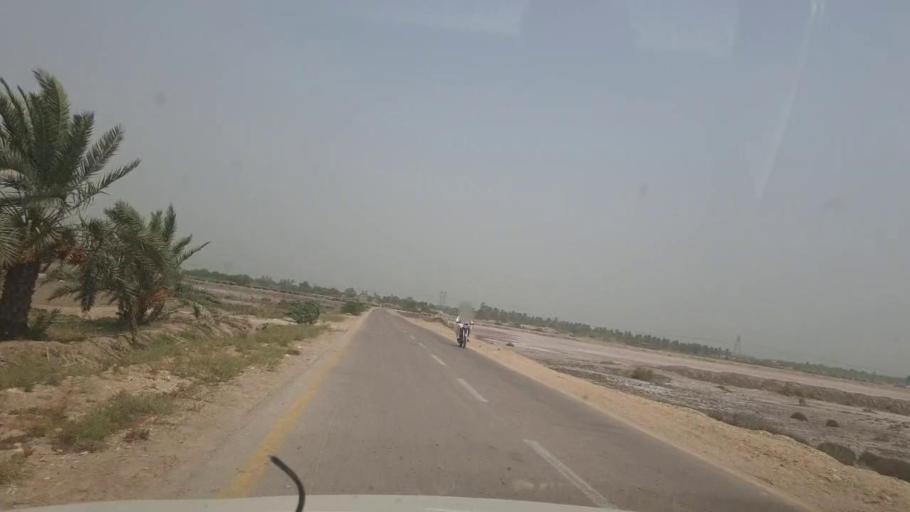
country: PK
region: Sindh
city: Kot Diji
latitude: 27.4013
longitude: 68.6601
